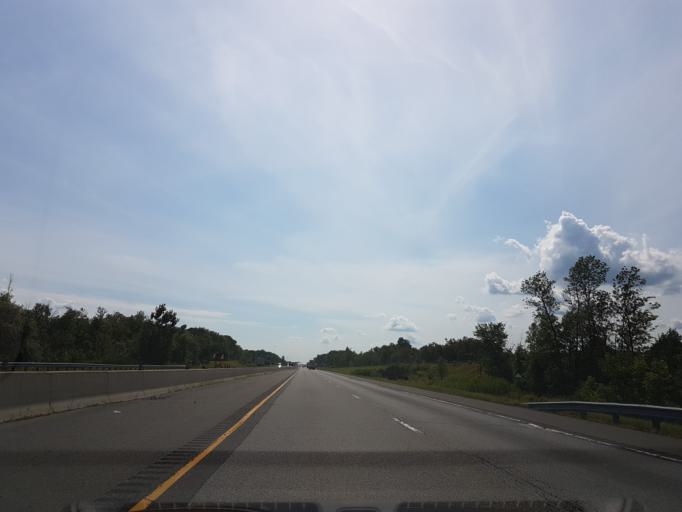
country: CA
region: Ontario
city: Prescott
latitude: 44.7472
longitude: -75.4893
